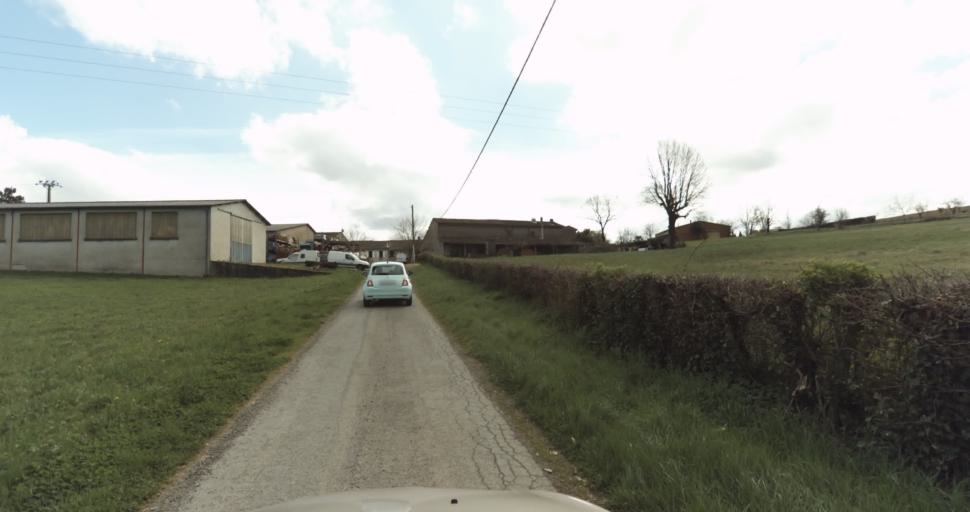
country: FR
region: Midi-Pyrenees
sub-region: Departement du Tarn
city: Puygouzon
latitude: 43.8959
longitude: 2.1459
